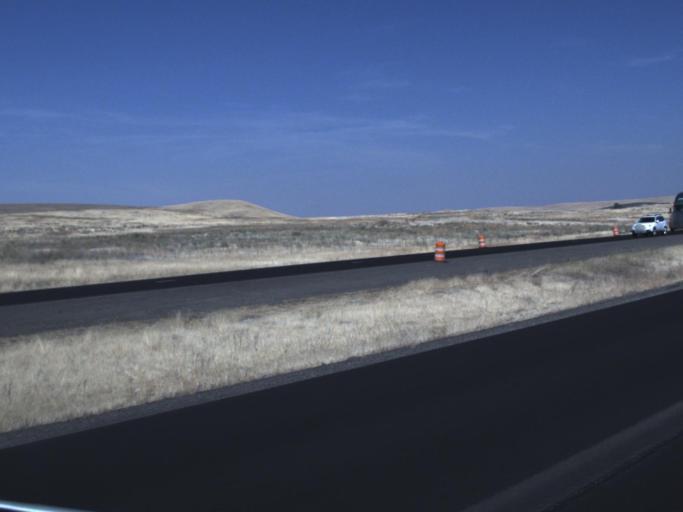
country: US
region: Washington
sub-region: Spokane County
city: Medical Lake
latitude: 47.3228
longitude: -117.9409
